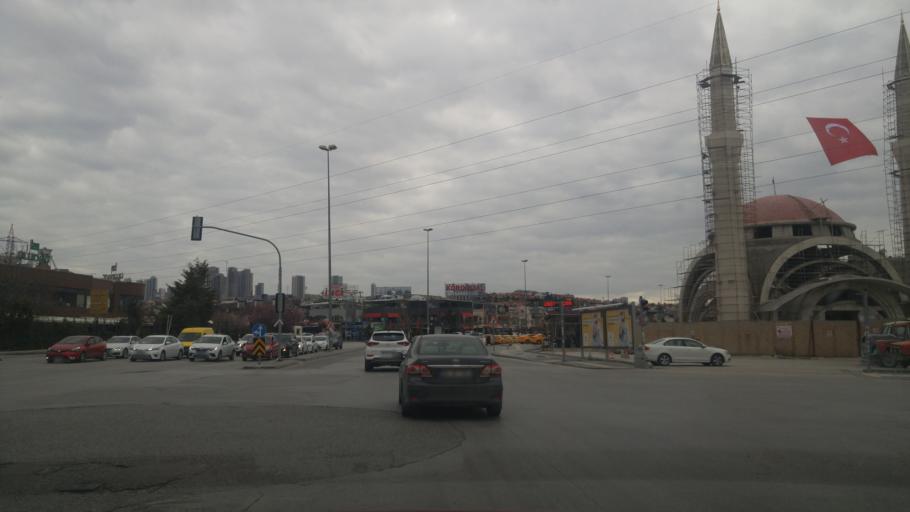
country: TR
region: Ankara
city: Etimesgut
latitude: 39.8740
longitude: 32.6878
